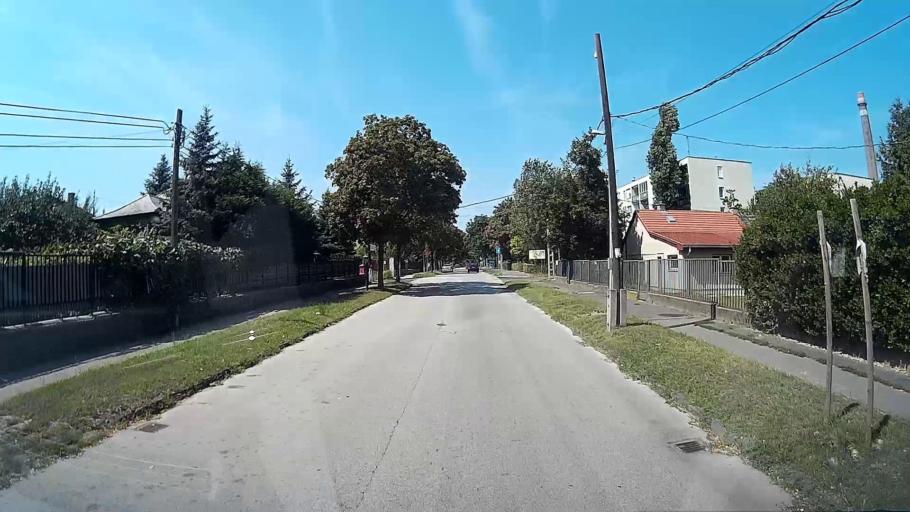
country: HU
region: Budapest
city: Budapest X. keruelet
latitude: 47.4828
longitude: 19.1501
